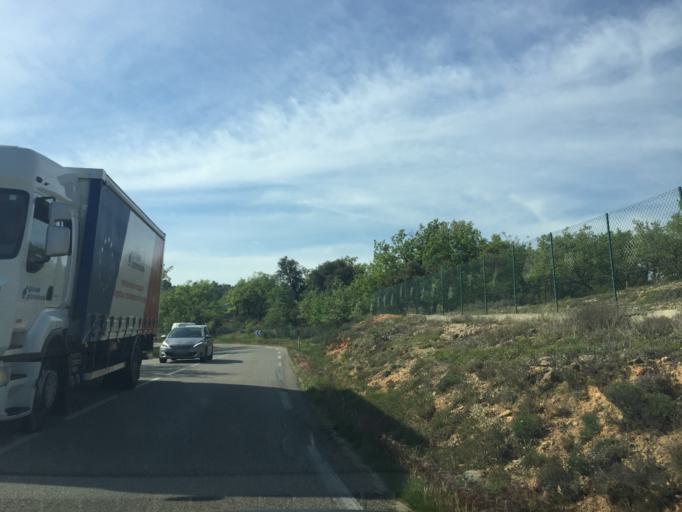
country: FR
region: Provence-Alpes-Cote d'Azur
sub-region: Departement du Var
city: Vinon-sur-Verdon
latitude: 43.7029
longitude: 5.8275
